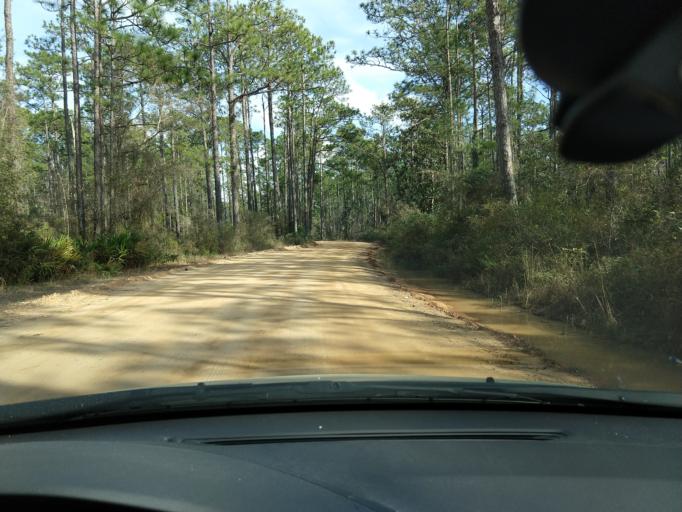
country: US
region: Florida
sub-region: Walton County
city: Seaside
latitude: 30.3680
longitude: -86.1275
